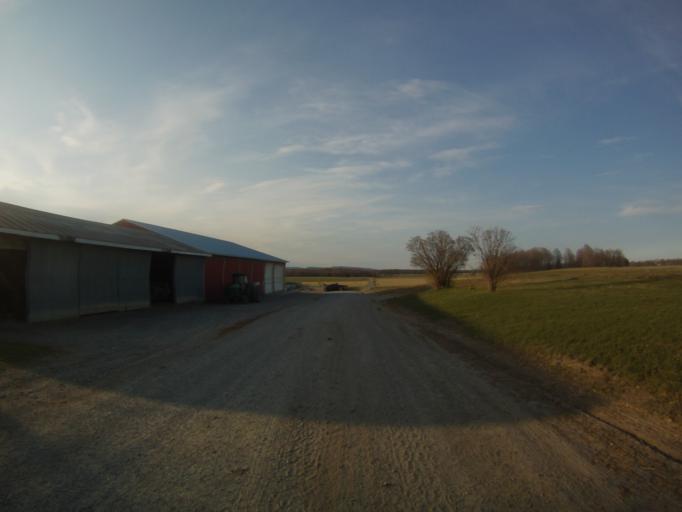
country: US
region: Vermont
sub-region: Addison County
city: Vergennes
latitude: 44.0931
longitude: -73.3116
